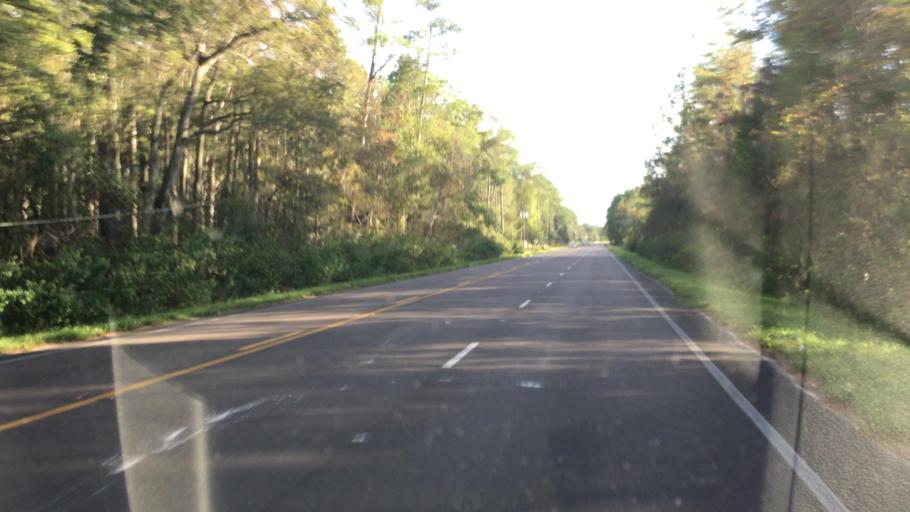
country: US
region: Florida
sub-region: Alachua County
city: Gainesville
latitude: 29.7111
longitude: -82.2773
